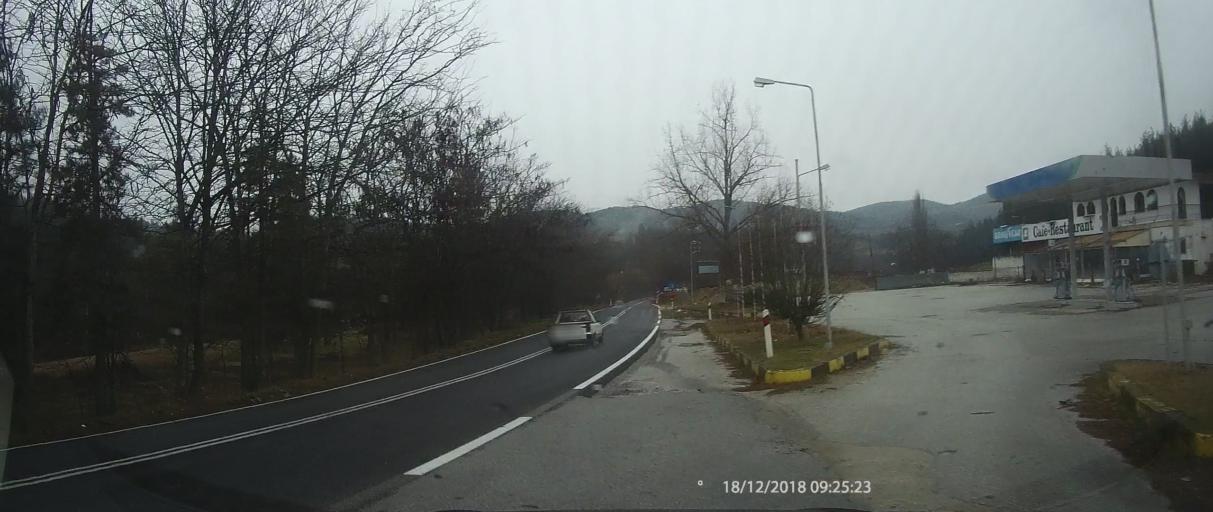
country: GR
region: Thessaly
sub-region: Nomos Larisis
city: Elassona
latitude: 39.9096
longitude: 22.1868
